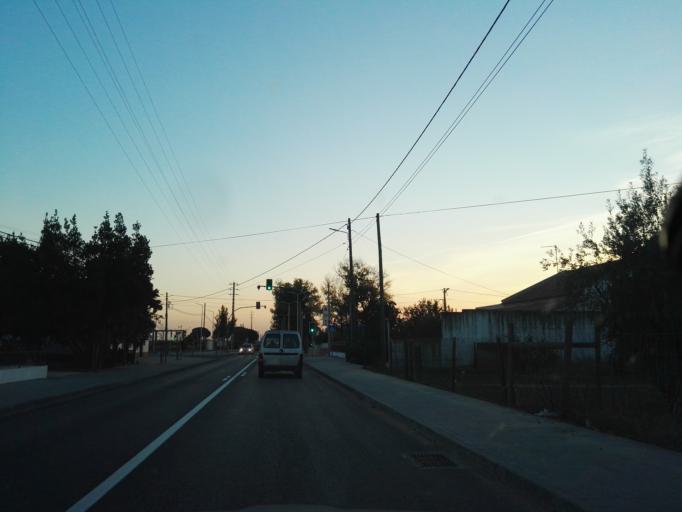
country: PT
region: Santarem
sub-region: Coruche
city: Coruche
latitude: 38.9549
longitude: -8.4928
